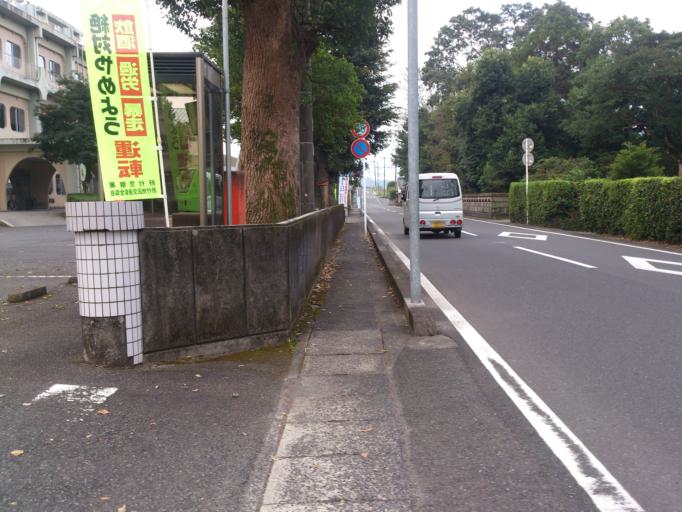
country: JP
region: Kagoshima
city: Kanoya
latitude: 31.3448
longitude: 130.9450
